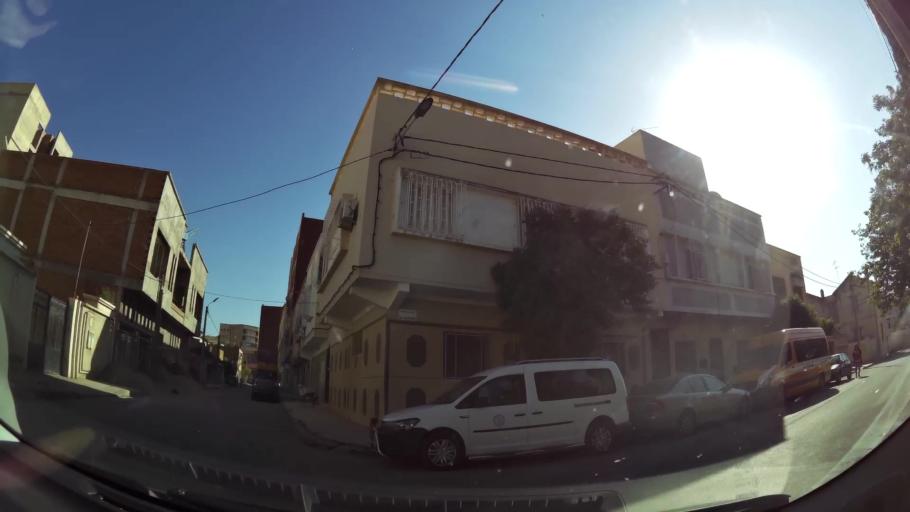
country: MA
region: Oriental
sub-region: Oujda-Angad
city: Oujda
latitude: 34.6837
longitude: -1.9194
